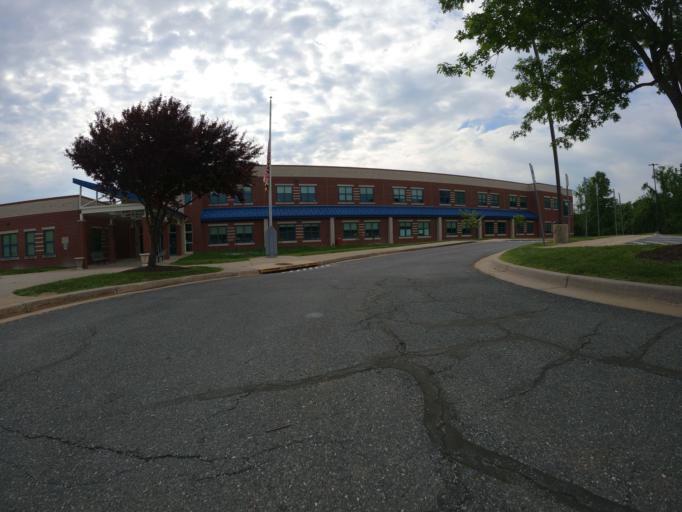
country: US
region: Maryland
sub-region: Howard County
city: Highland
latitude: 39.2409
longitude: -76.9843
